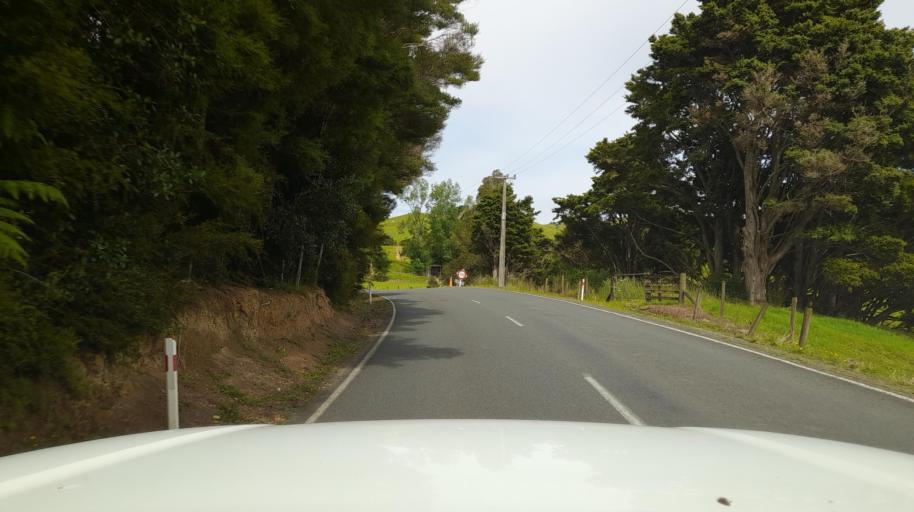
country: NZ
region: Northland
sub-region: Far North District
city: Taipa
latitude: -35.2695
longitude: 173.4932
